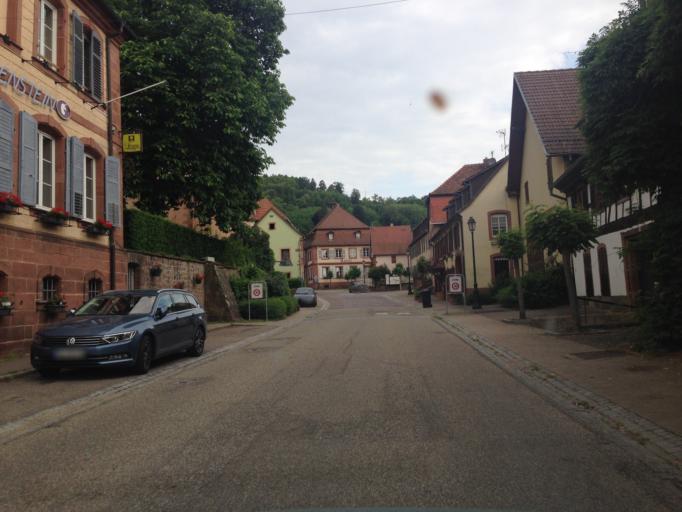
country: FR
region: Alsace
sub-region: Departement du Bas-Rhin
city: Neuwiller-les-Saverne
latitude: 48.8235
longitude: 7.4065
